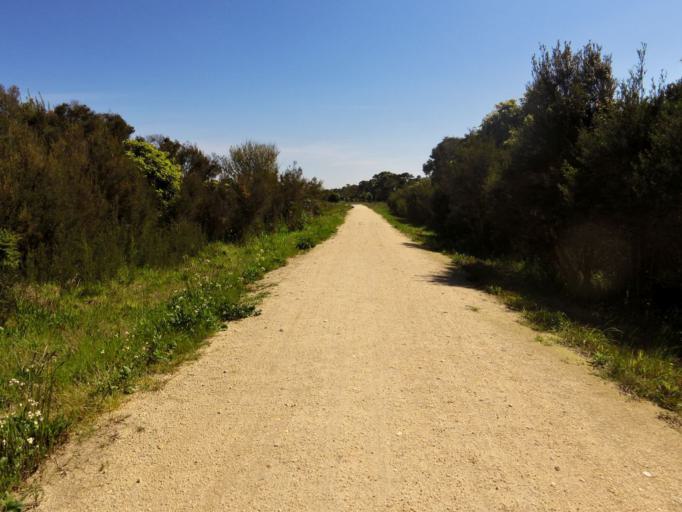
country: AU
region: Victoria
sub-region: Latrobe
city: Morwell
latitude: -38.6658
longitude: 146.3127
